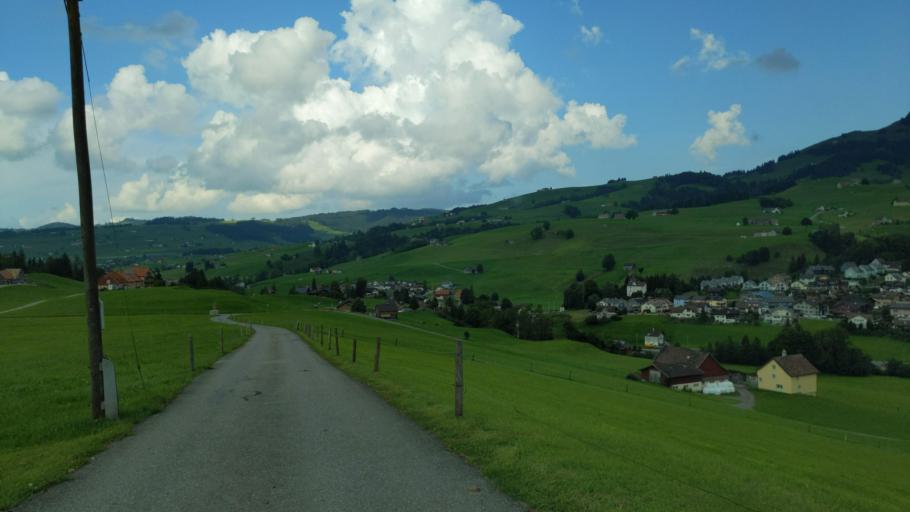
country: CH
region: Appenzell Innerrhoden
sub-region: Appenzell Inner Rhodes
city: Appenzell
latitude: 47.3032
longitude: 9.4293
